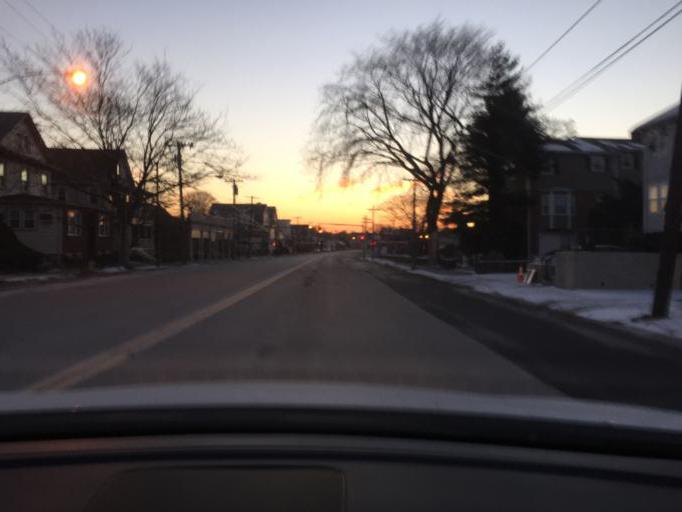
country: US
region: Massachusetts
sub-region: Middlesex County
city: Watertown
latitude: 42.3765
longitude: -71.1600
